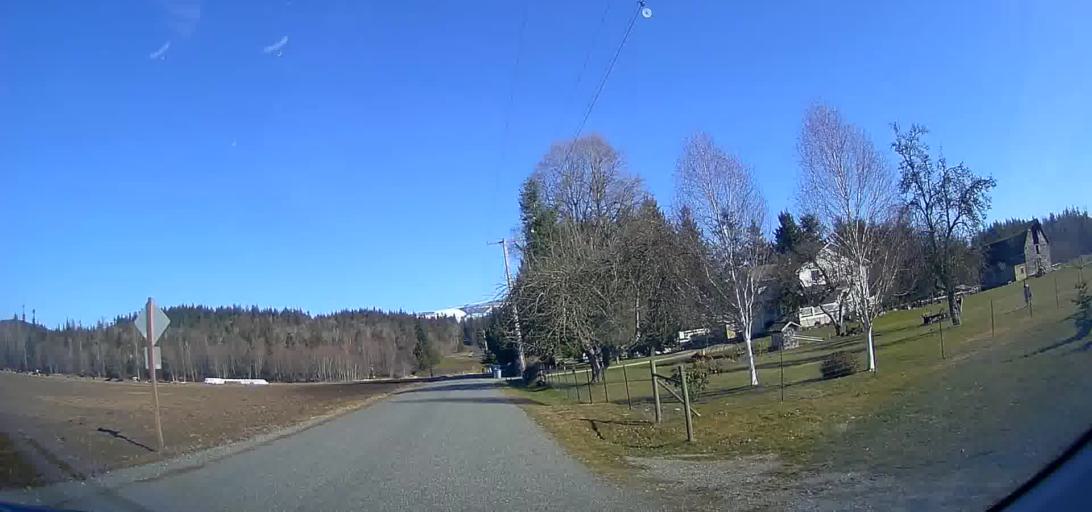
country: US
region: Washington
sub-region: Skagit County
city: Clear Lake
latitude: 48.4495
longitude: -122.2619
